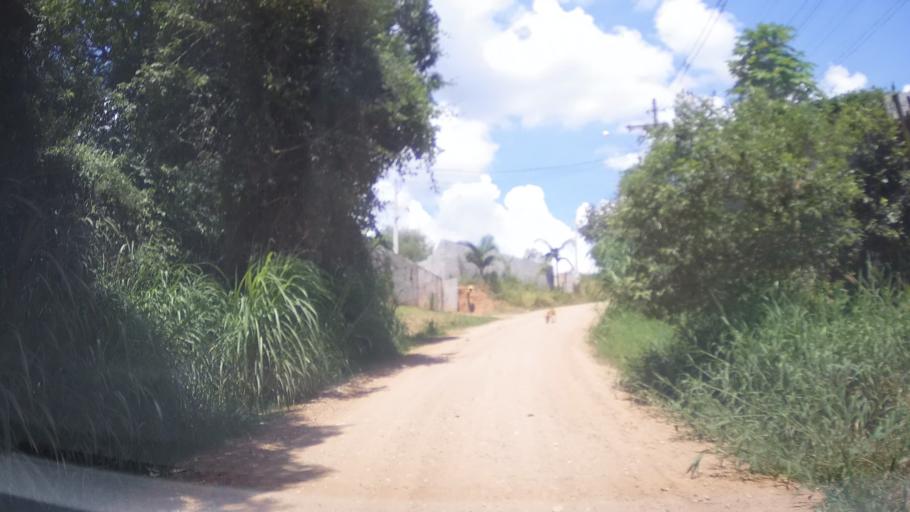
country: BR
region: Sao Paulo
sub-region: Jarinu
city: Jarinu
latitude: -23.1234
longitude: -46.8052
